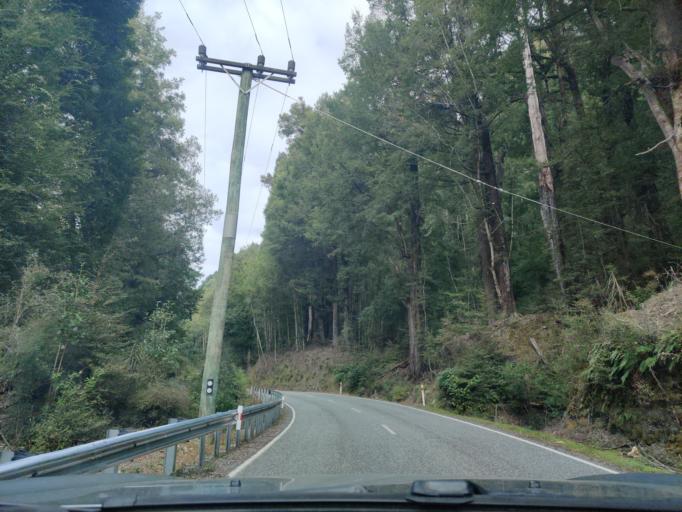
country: NZ
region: Otago
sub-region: Queenstown-Lakes District
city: Queenstown
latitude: -45.0710
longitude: 168.4994
